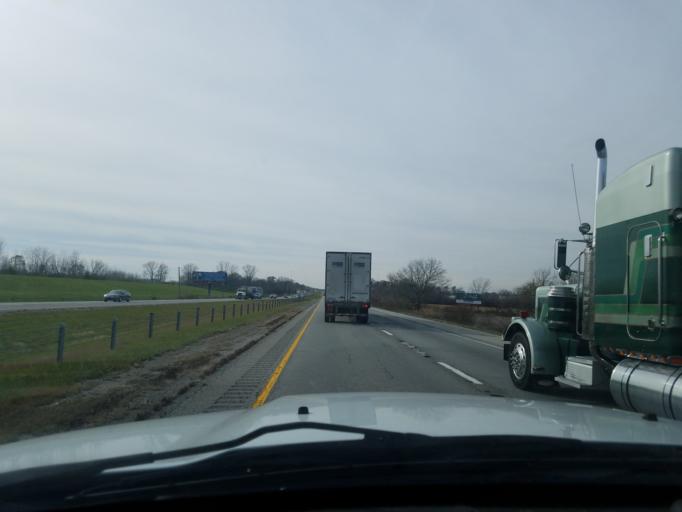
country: US
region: Indiana
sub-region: Madison County
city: Pendleton
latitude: 40.0412
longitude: -85.7095
